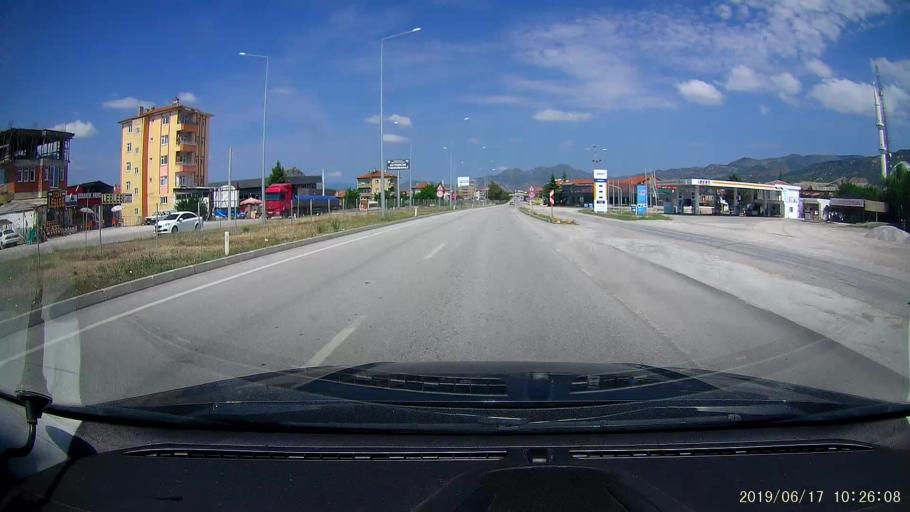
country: TR
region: Corum
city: Osmancik
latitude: 40.9718
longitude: 34.8229
